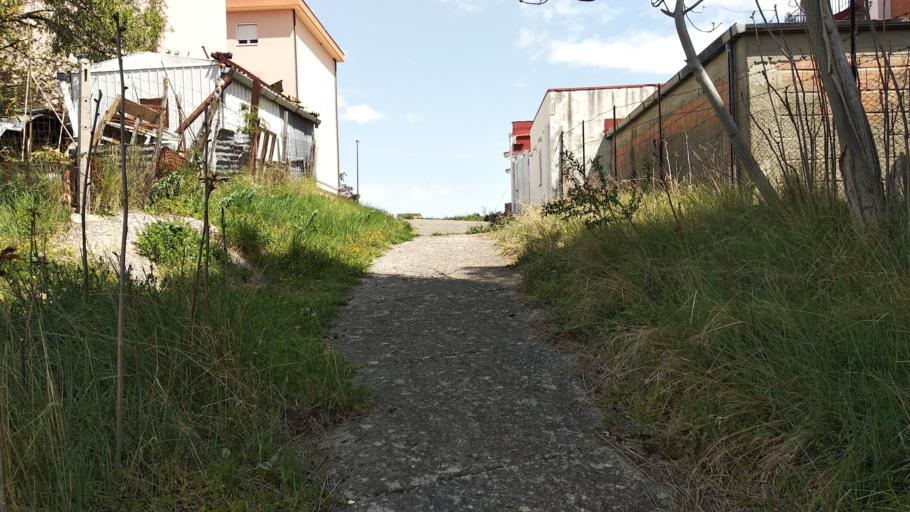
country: IT
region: Basilicate
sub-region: Provincia di Matera
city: Tricarico
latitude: 40.6145
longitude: 16.1412
